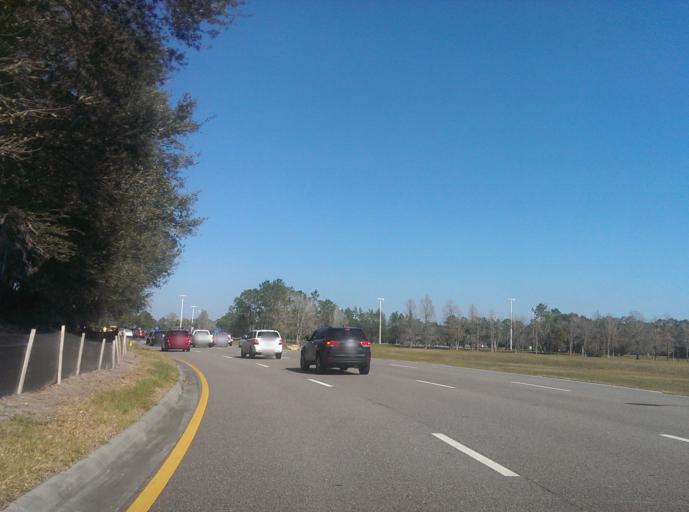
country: US
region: Florida
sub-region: Osceola County
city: Celebration
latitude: 28.3959
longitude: -81.5746
